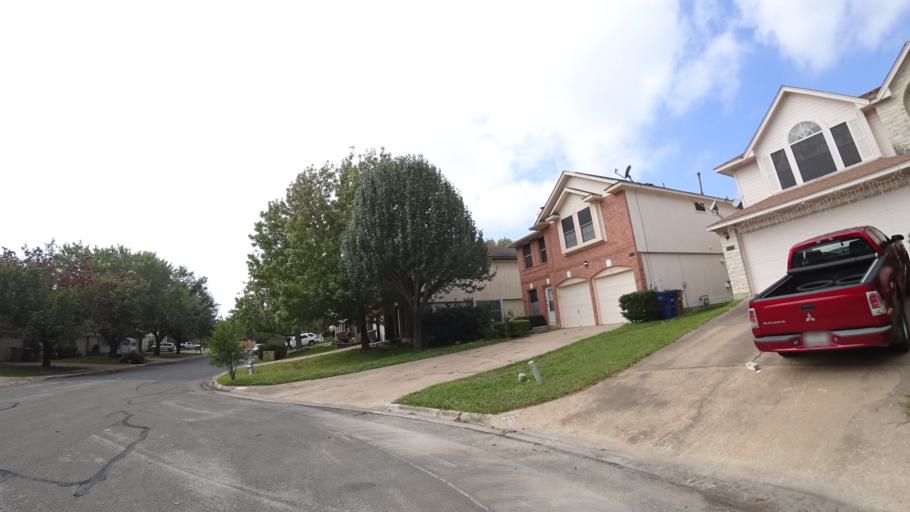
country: US
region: Texas
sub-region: Travis County
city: Shady Hollow
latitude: 30.1955
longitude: -97.8340
